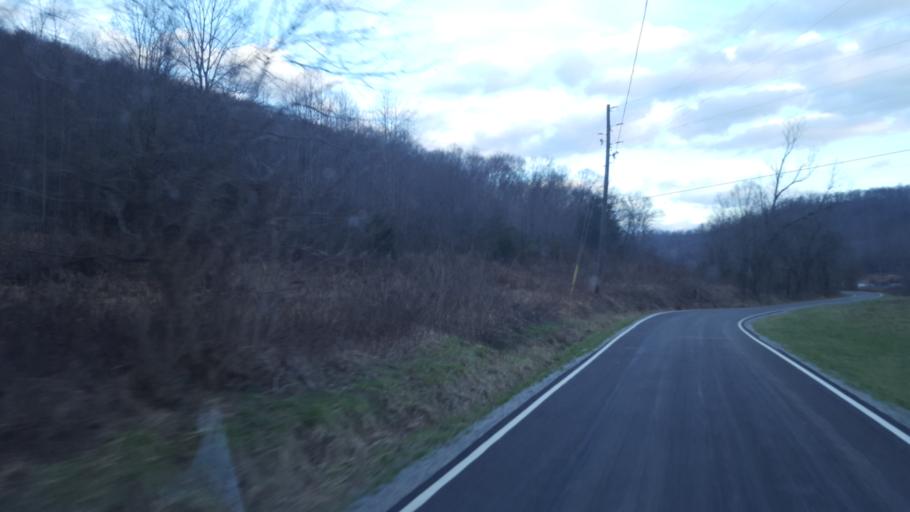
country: US
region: Kentucky
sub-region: Lewis County
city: Vanceburg
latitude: 38.5117
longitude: -83.5043
